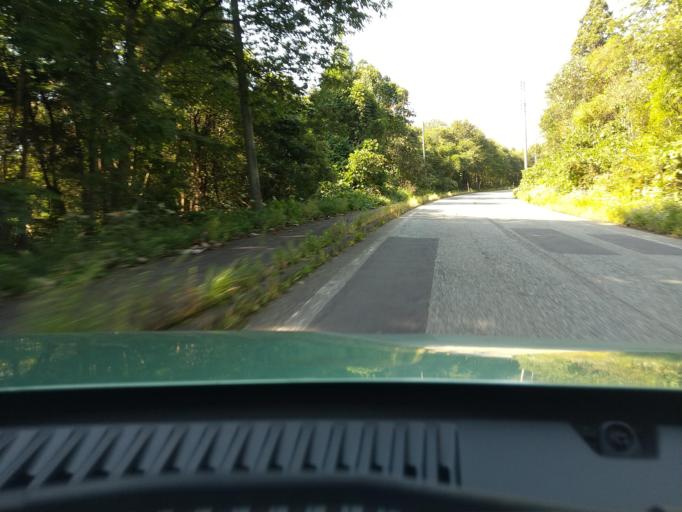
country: JP
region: Akita
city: Omagari
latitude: 39.5979
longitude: 140.3130
